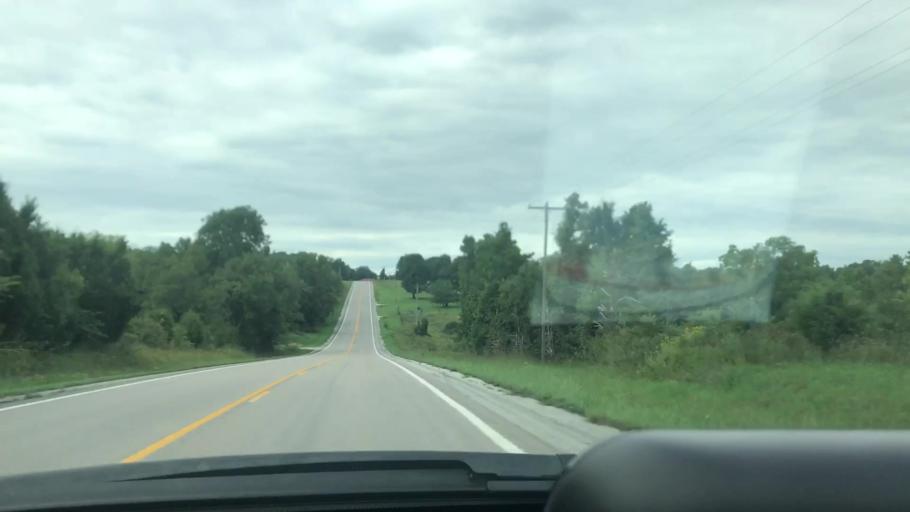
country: US
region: Missouri
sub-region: Benton County
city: Warsaw
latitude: 38.1493
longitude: -93.2930
